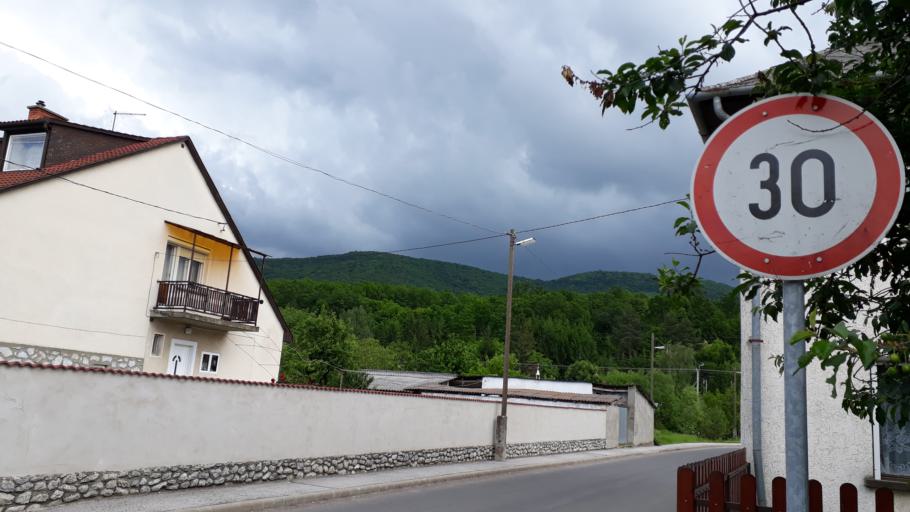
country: HU
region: Heves
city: Felsotarkany
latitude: 47.9783
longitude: 20.4256
